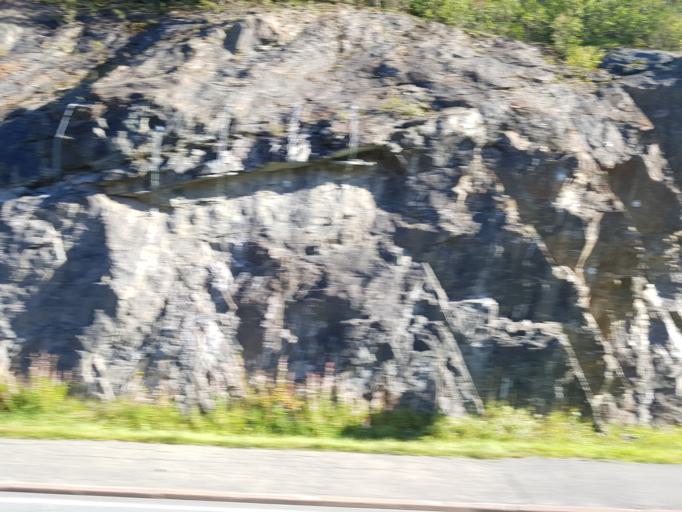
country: NO
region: Sor-Trondelag
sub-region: Skaun
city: Borsa
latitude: 63.4487
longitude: 10.1936
